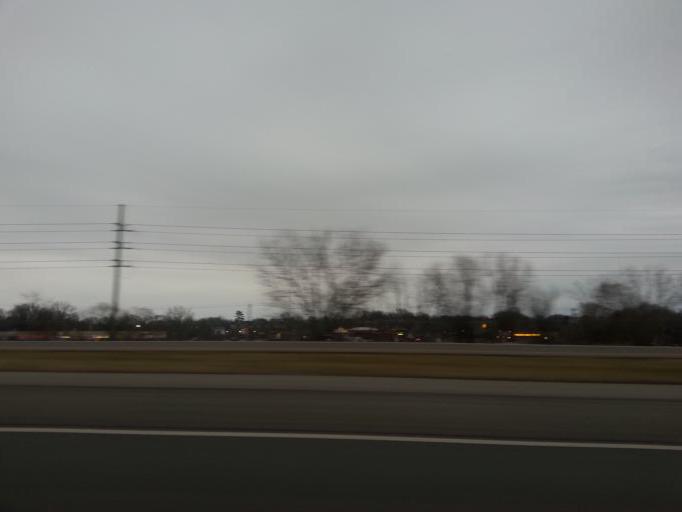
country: US
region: Iowa
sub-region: Linn County
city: Hiawatha
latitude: 42.0190
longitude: -91.6670
